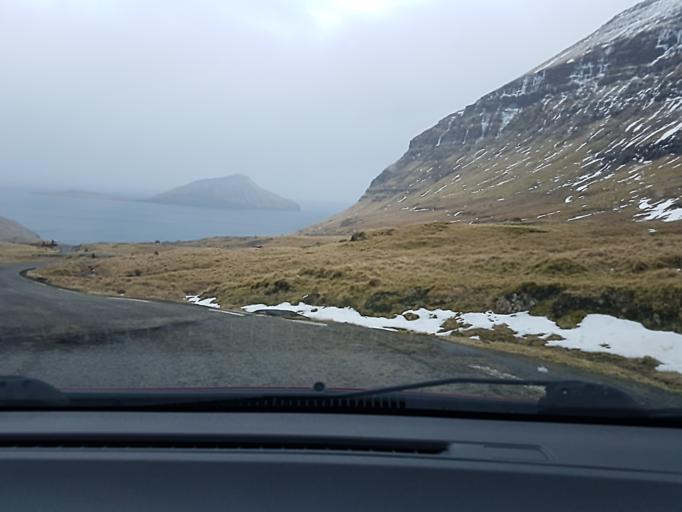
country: FO
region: Streymoy
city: Kollafjordhur
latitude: 62.0538
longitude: -6.9207
